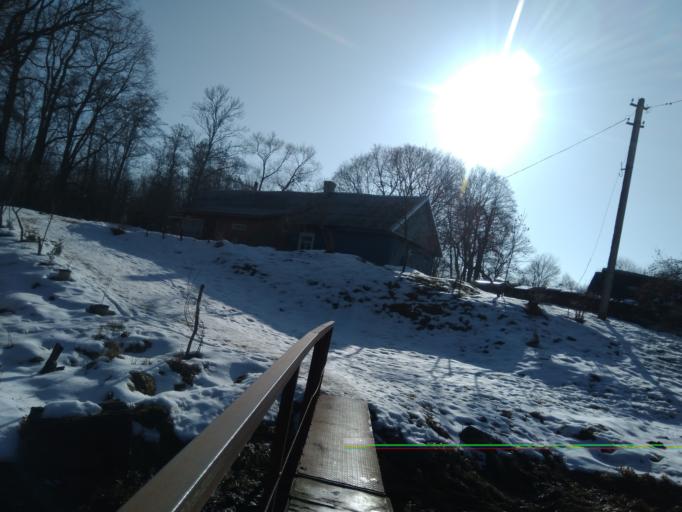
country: BY
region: Minsk
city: Nyasvizh
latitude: 53.2020
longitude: 26.6432
